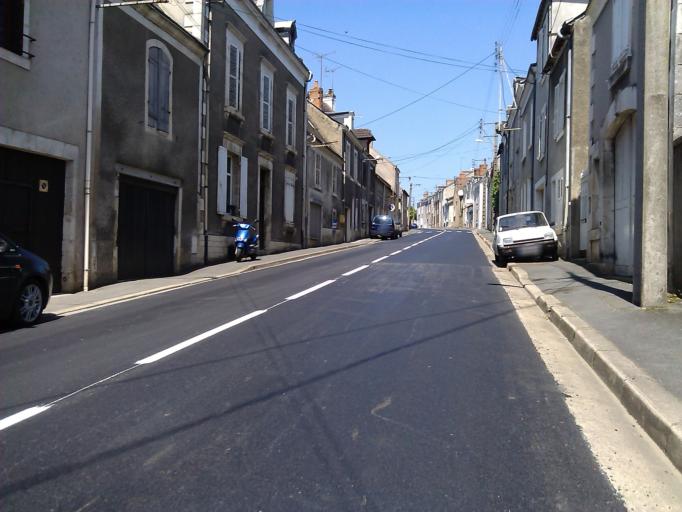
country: FR
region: Centre
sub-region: Departement de l'Indre
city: Saint-Marcel
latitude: 46.6021
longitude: 1.5118
